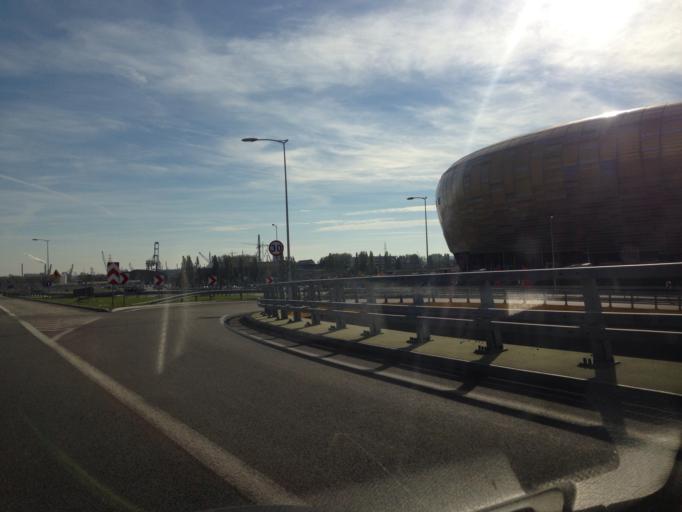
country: PL
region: Pomeranian Voivodeship
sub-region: Gdansk
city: Gdansk
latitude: 54.3924
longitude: 18.6412
